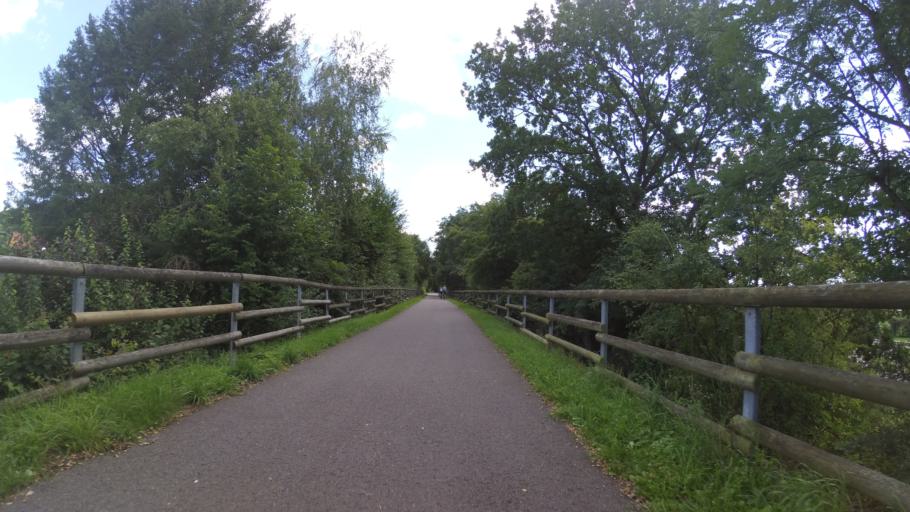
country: DE
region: Saarland
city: Namborn
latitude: 49.4955
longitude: 7.1241
